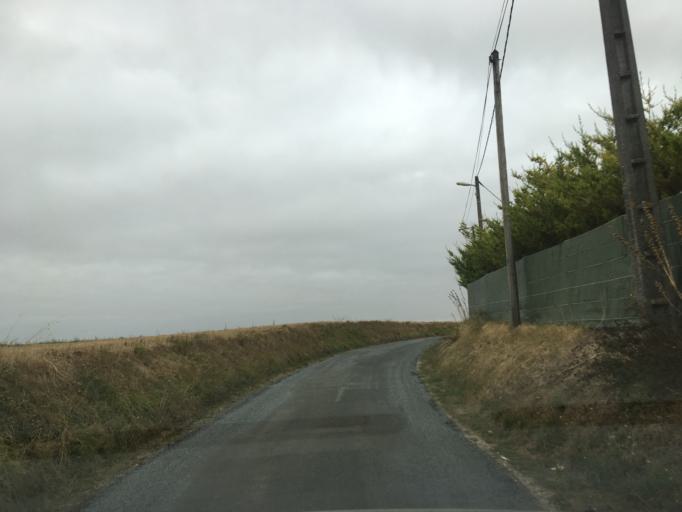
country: FR
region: Poitou-Charentes
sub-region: Departement des Deux-Sevres
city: Beauvoir-sur-Niort
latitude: 46.0793
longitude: -0.4944
